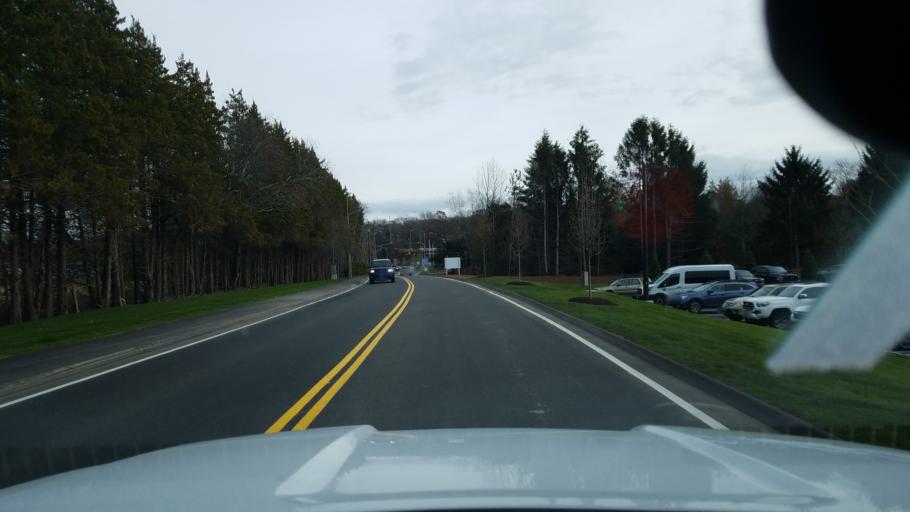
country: US
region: Connecticut
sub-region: New London County
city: Niantic
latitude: 41.3610
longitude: -72.2140
